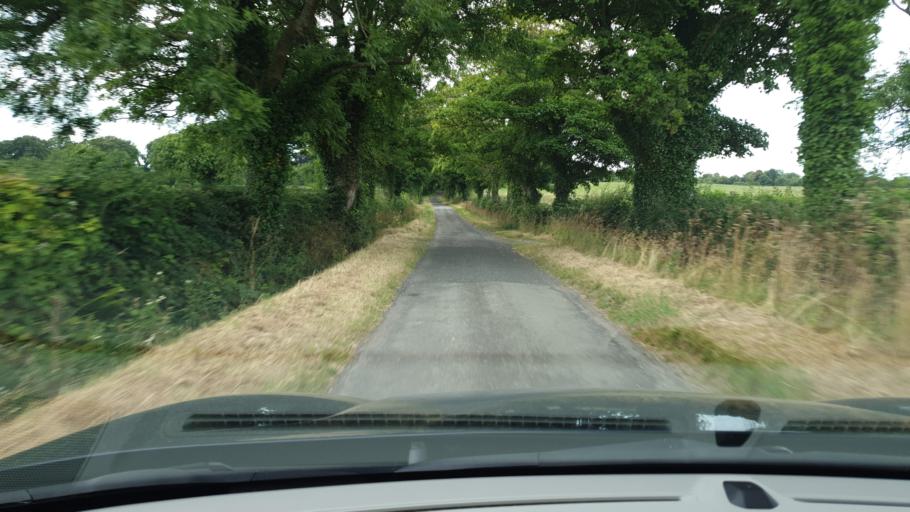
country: IE
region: Leinster
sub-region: An Mhi
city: Ashbourne
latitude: 53.5474
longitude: -6.3870
